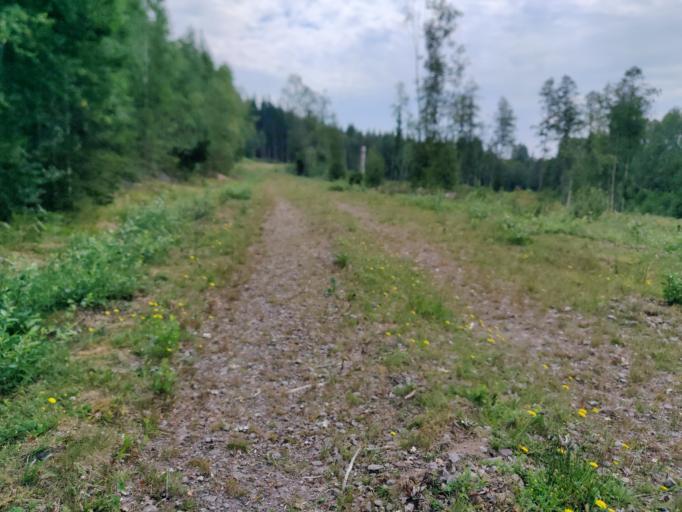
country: SE
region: Vaermland
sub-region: Hagfors Kommun
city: Hagfors
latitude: 59.9626
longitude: 13.5731
